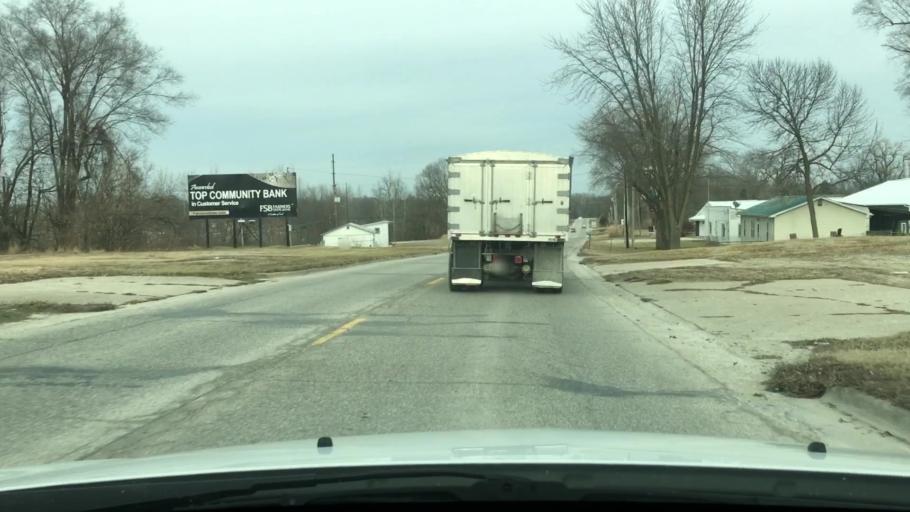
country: US
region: Illinois
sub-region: Pike County
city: Pittsfield
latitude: 39.6154
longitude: -90.8029
